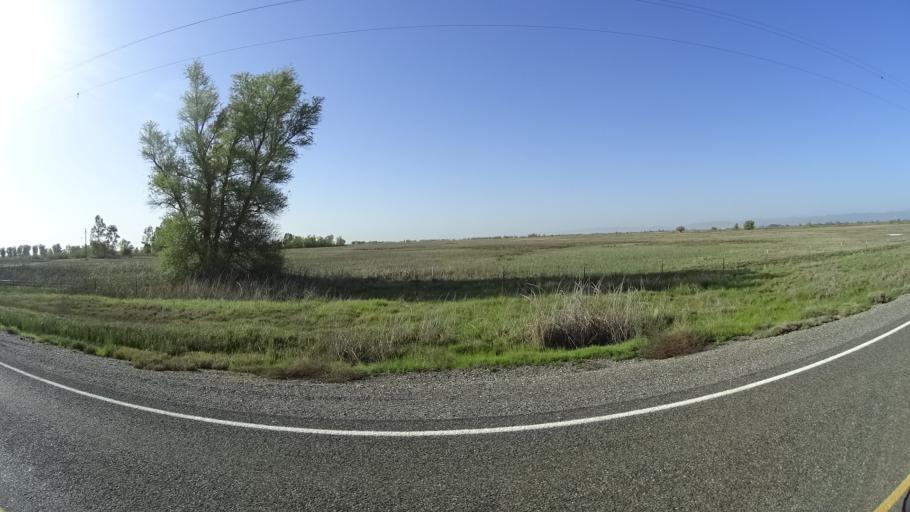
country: US
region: California
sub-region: Glenn County
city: Willows
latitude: 39.4077
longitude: -122.1375
